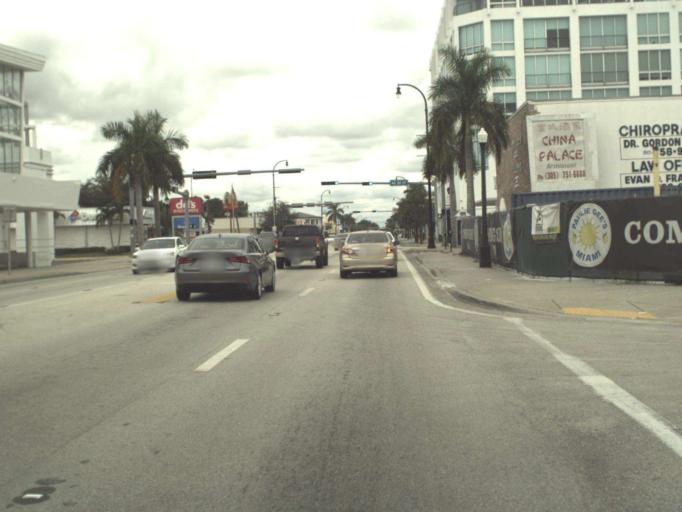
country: US
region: Florida
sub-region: Miami-Dade County
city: El Portal
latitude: 25.8486
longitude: -80.1846
